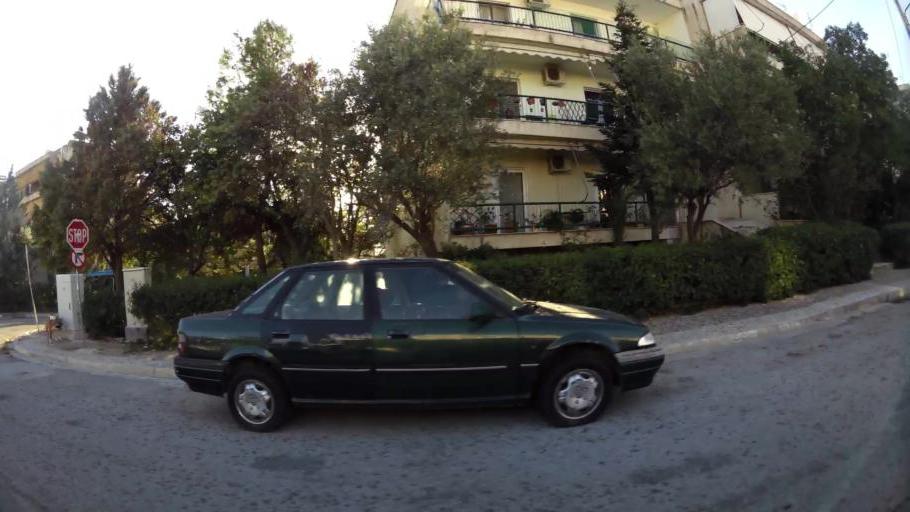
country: GR
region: Attica
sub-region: Nomarchia Anatolikis Attikis
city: Acharnes
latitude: 38.0844
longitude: 23.7211
